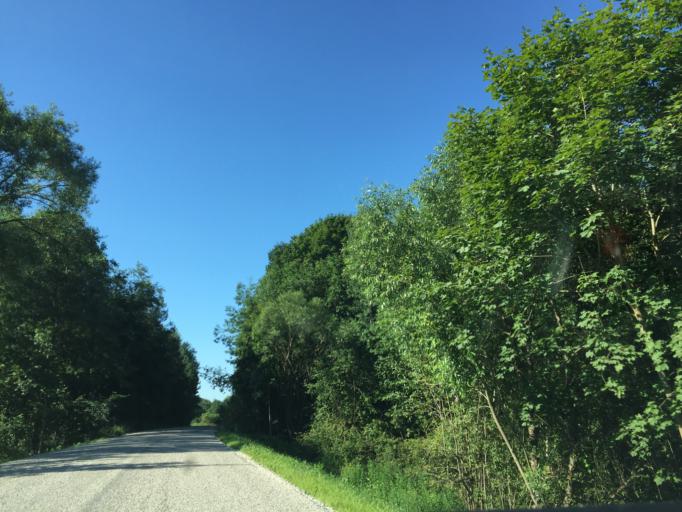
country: LV
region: Vilanu
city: Vilani
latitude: 56.5733
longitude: 26.9285
